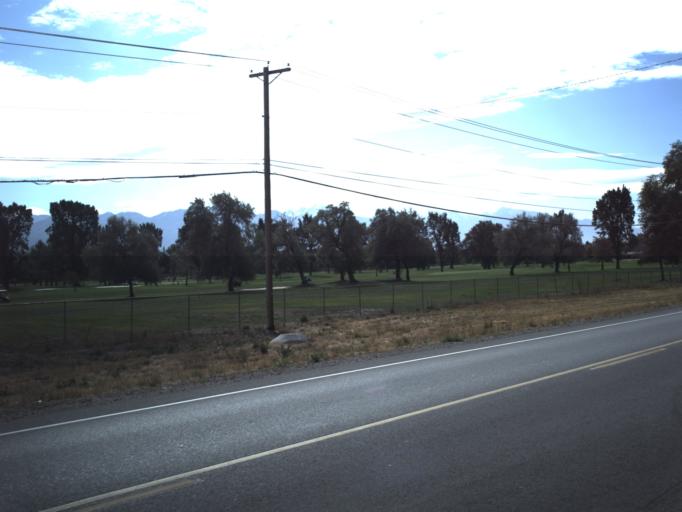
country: US
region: Utah
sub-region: Davis County
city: North Salt Lake
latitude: 40.8047
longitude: -111.9392
